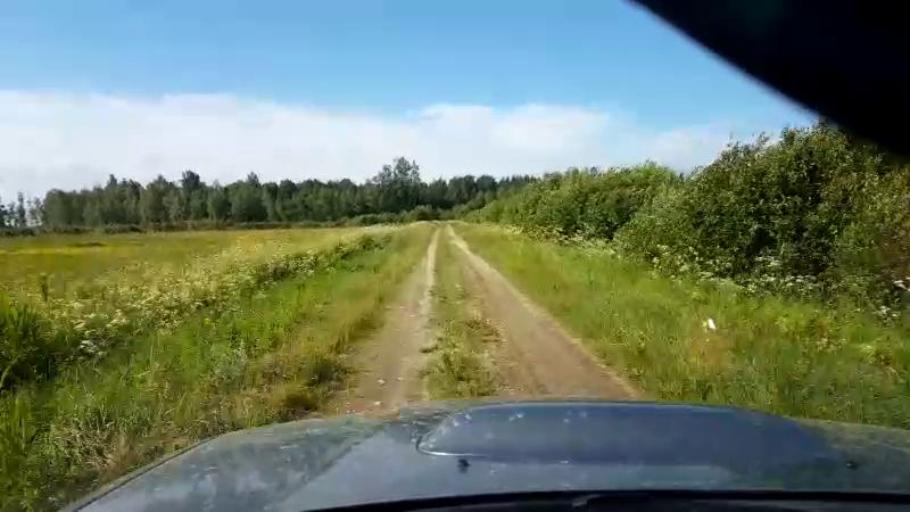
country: EE
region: Paernumaa
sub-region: Sindi linn
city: Sindi
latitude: 58.5052
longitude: 24.6416
